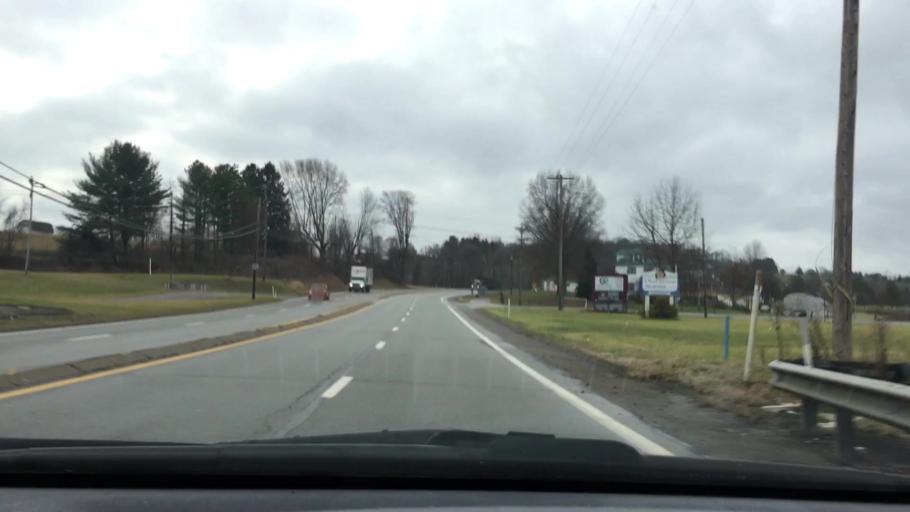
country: US
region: Pennsylvania
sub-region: Westmoreland County
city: West Newton
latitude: 40.1496
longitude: -79.7729
